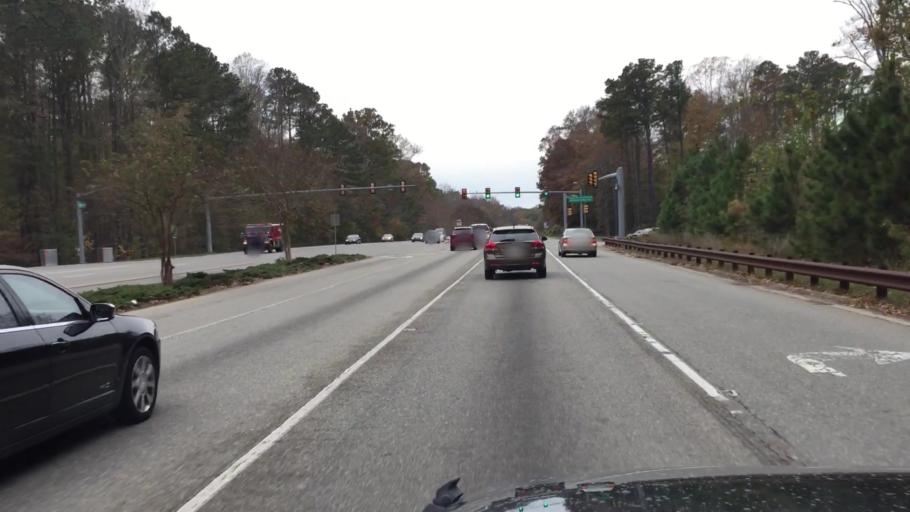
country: US
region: Virginia
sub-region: City of Williamsburg
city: Williamsburg
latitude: 37.2473
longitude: -76.6813
